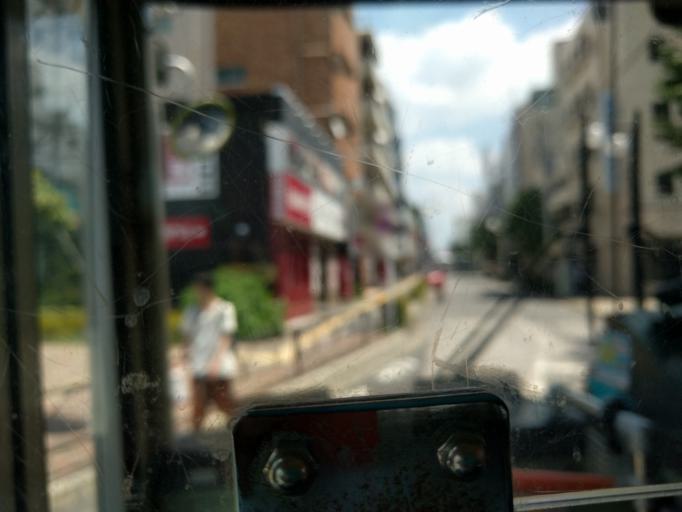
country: JP
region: Tokyo
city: Chofugaoka
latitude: 35.6391
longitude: 139.5977
